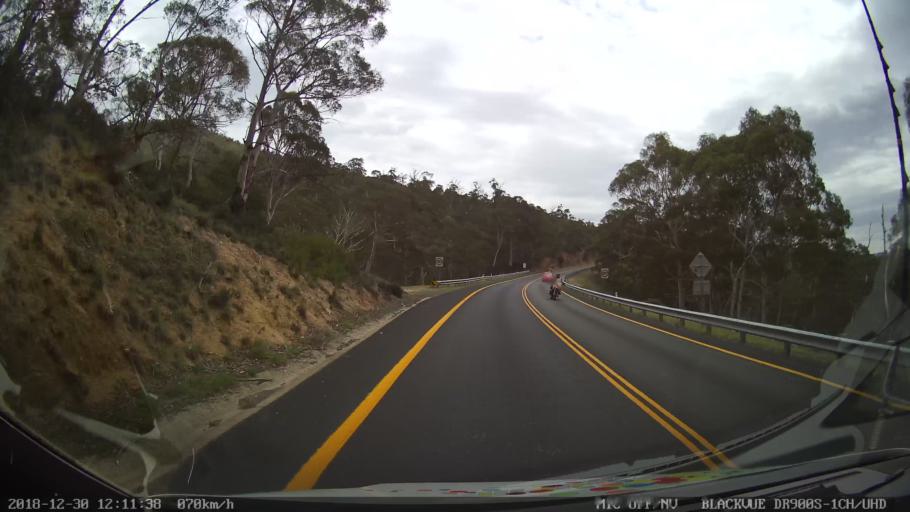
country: AU
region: New South Wales
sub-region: Snowy River
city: Jindabyne
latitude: -36.3647
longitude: 148.5869
